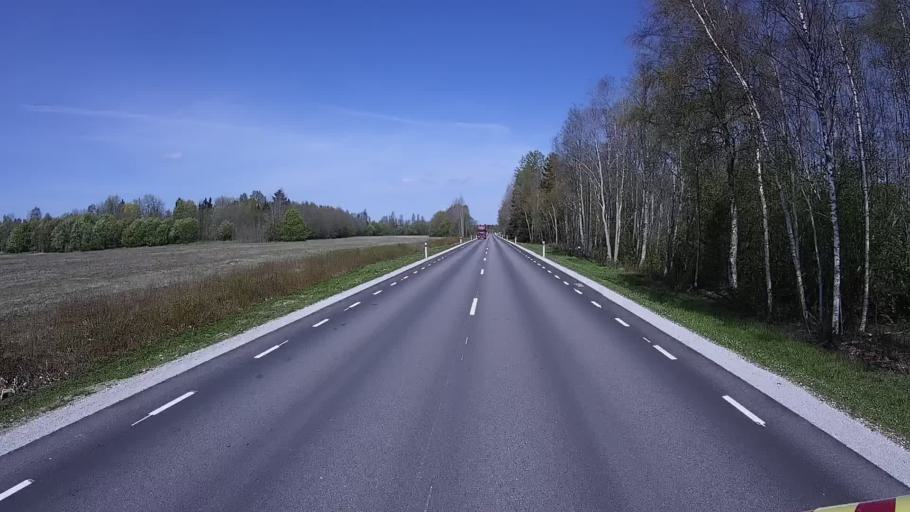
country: EE
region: Harju
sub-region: Nissi vald
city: Turba
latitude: 59.1639
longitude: 24.0742
